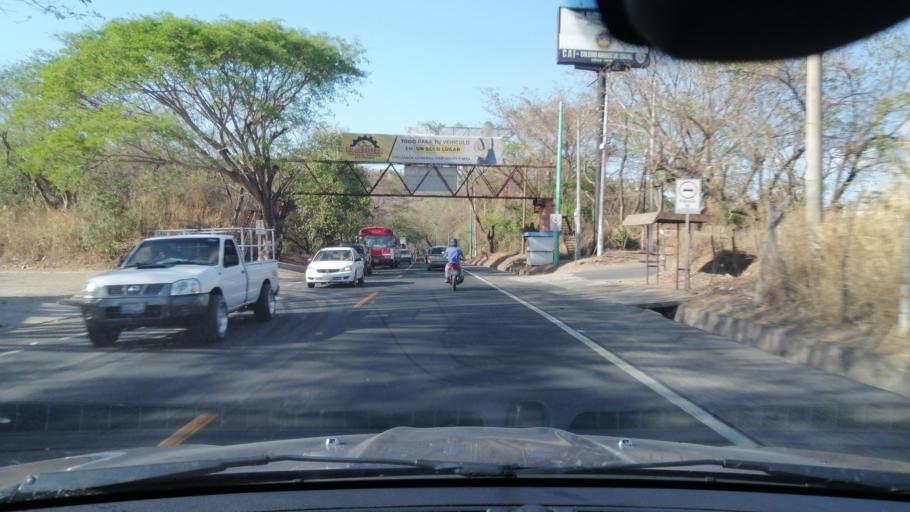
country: SV
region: Santa Ana
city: Santa Ana
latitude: 14.0053
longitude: -89.5419
